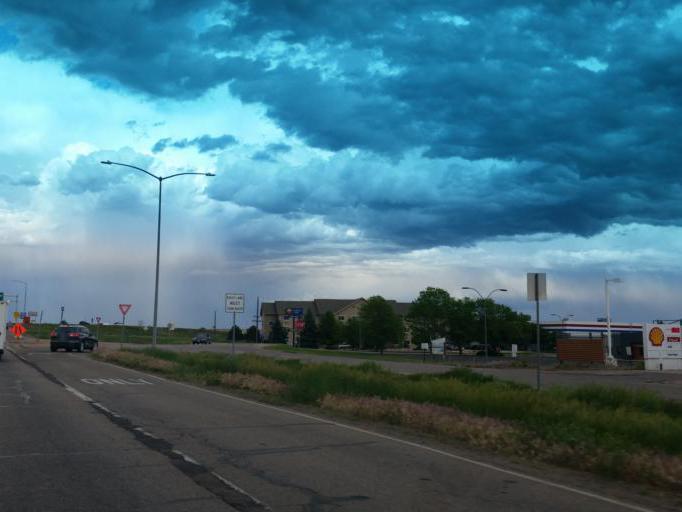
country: US
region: Colorado
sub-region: Larimer County
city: Fort Collins
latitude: 40.5810
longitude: -105.0064
